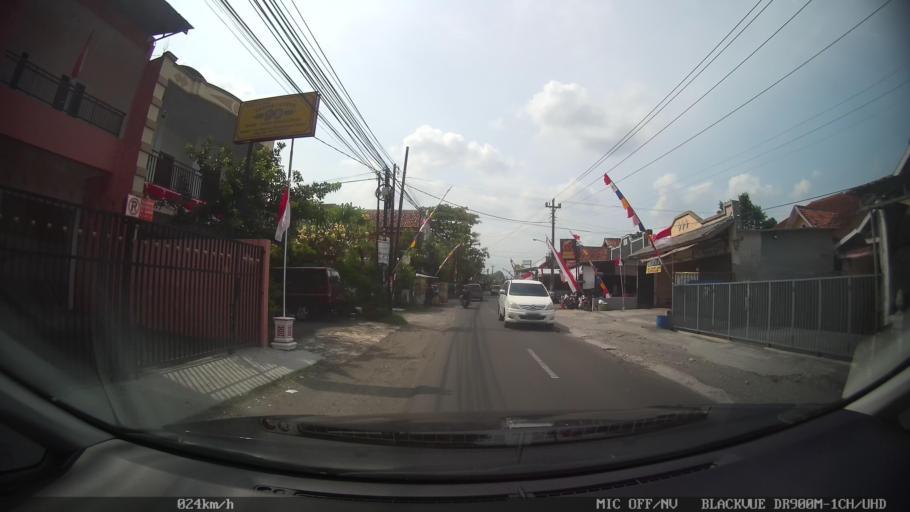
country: ID
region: Daerah Istimewa Yogyakarta
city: Depok
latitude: -7.8020
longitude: 110.4162
